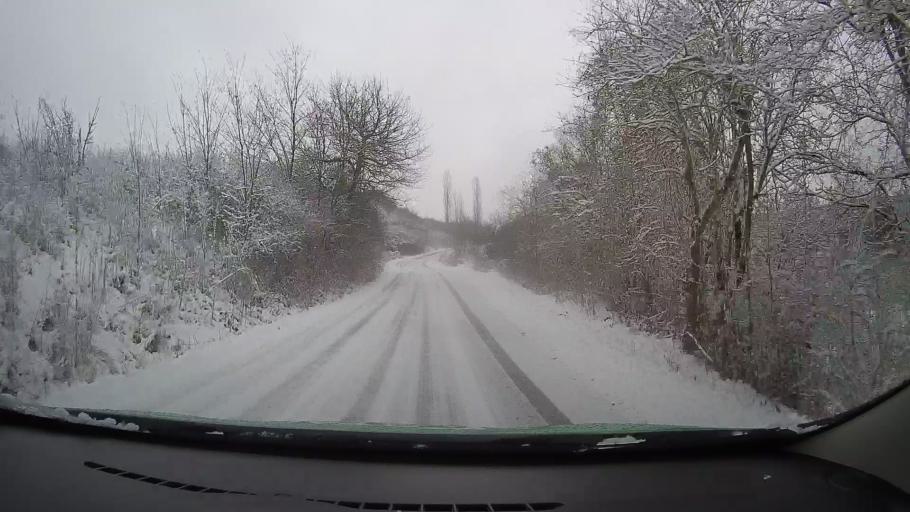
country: RO
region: Hunedoara
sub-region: Comuna Pestisu Mic
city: Pestisu Mic
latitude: 45.8180
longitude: 22.8844
